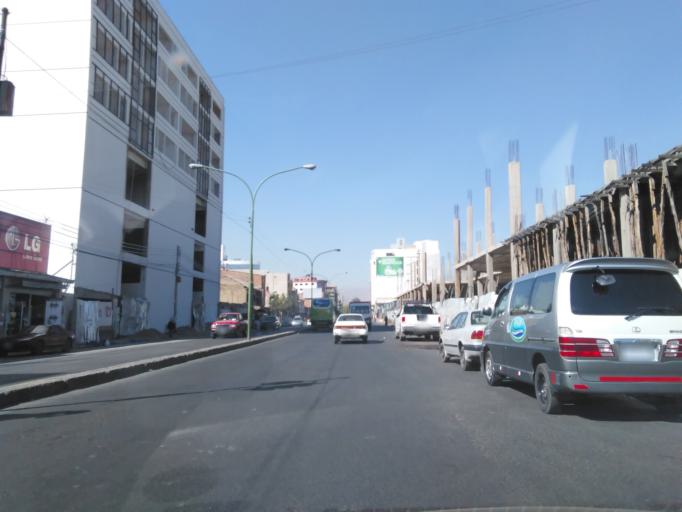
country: BO
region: Cochabamba
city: Cochabamba
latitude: -17.4040
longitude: -66.1572
